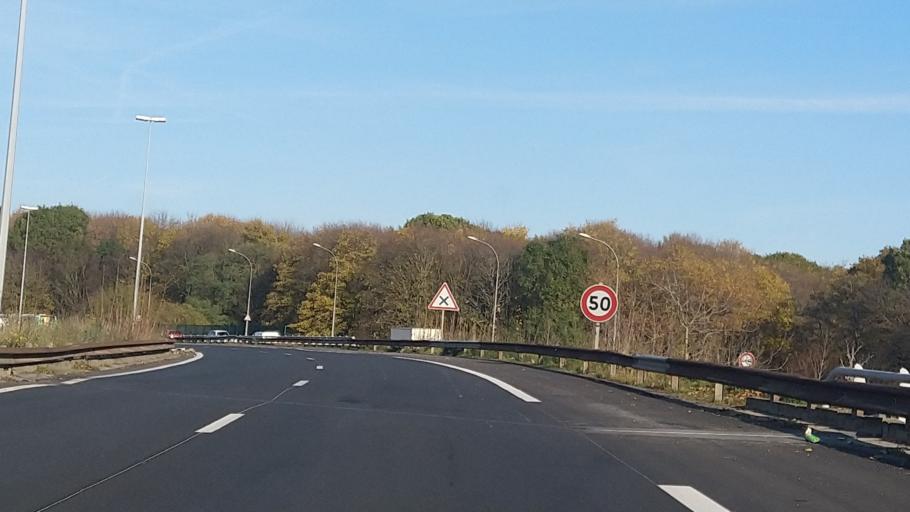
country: FR
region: Ile-de-France
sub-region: Departement de Seine-Saint-Denis
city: La Courneuve
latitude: 48.9353
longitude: 2.3877
